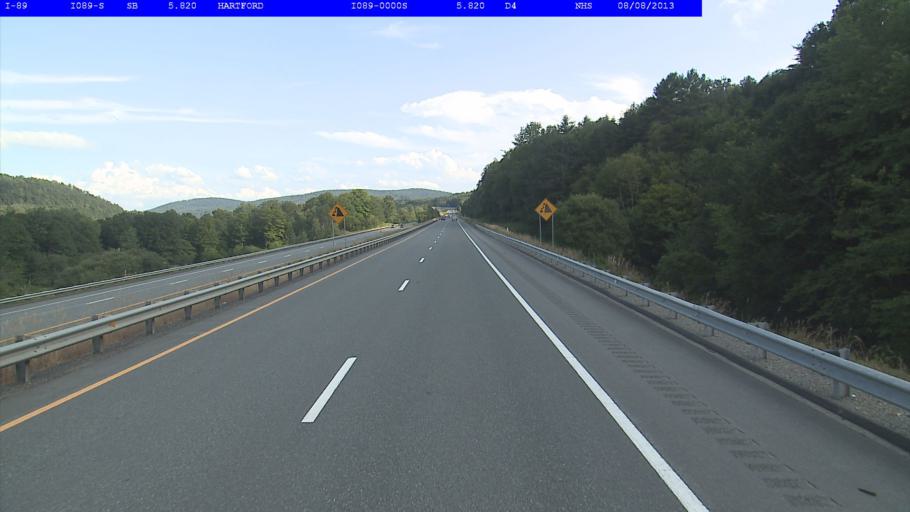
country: US
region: Vermont
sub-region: Windsor County
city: White River Junction
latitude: 43.6896
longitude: -72.4047
